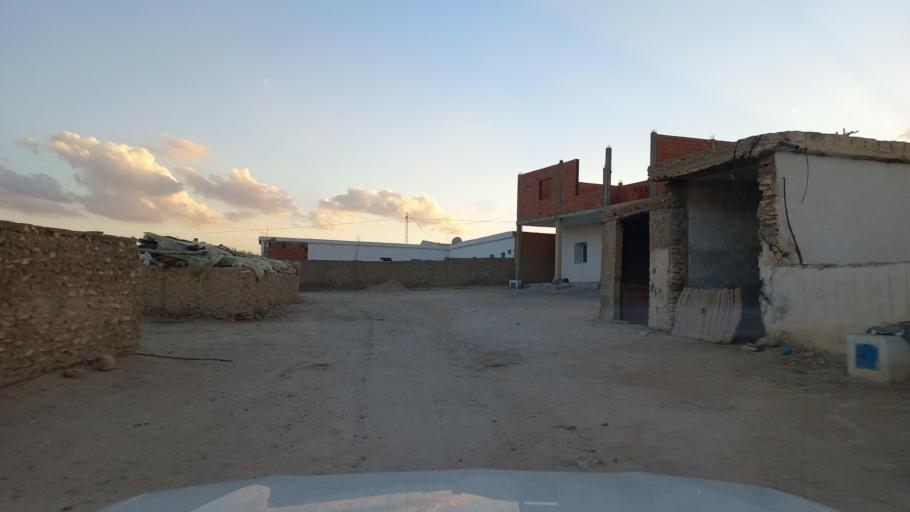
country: TN
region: Al Qasrayn
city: Sbiba
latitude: 35.3679
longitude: 9.0690
